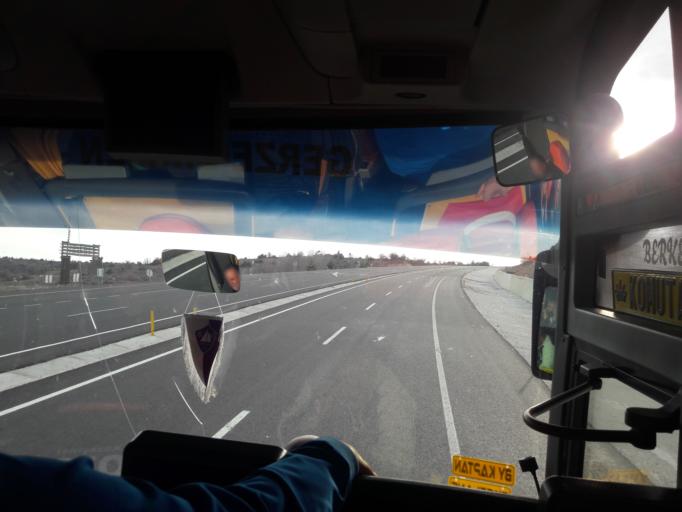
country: TR
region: Cankiri
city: Ilgaz
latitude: 40.8596
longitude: 33.6242
